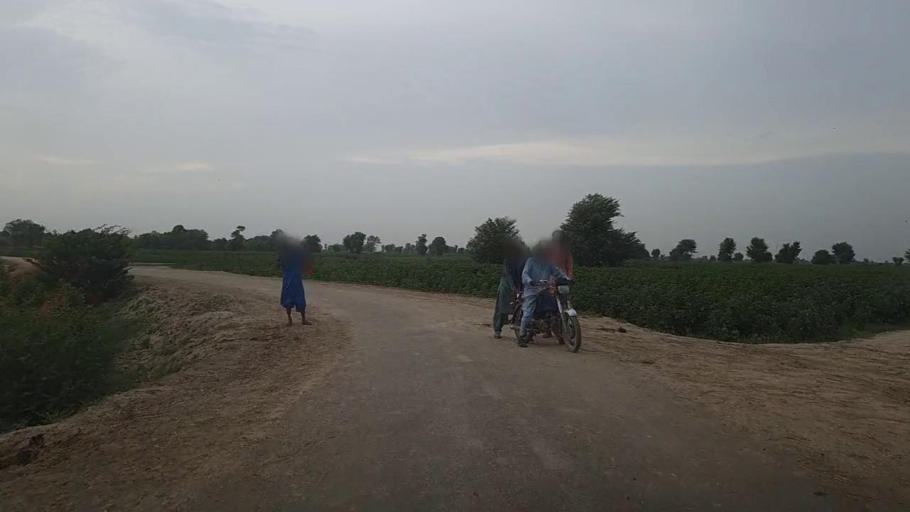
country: PK
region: Sindh
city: Karaundi
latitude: 26.9570
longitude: 68.3621
